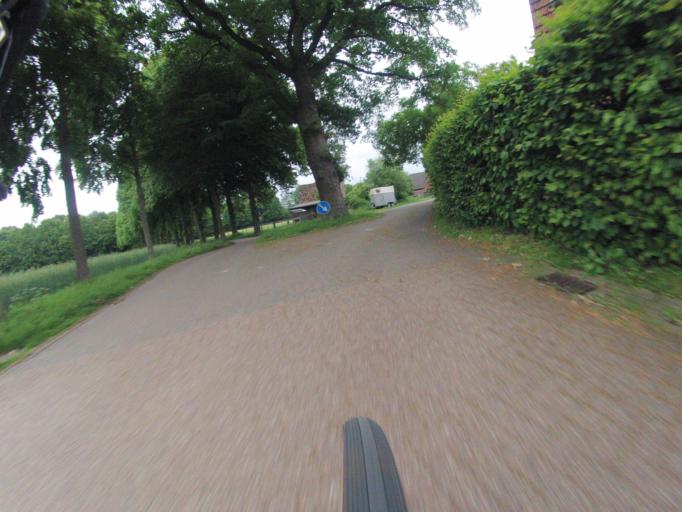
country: DE
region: North Rhine-Westphalia
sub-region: Regierungsbezirk Munster
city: Horstel
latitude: 52.2700
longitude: 7.5769
